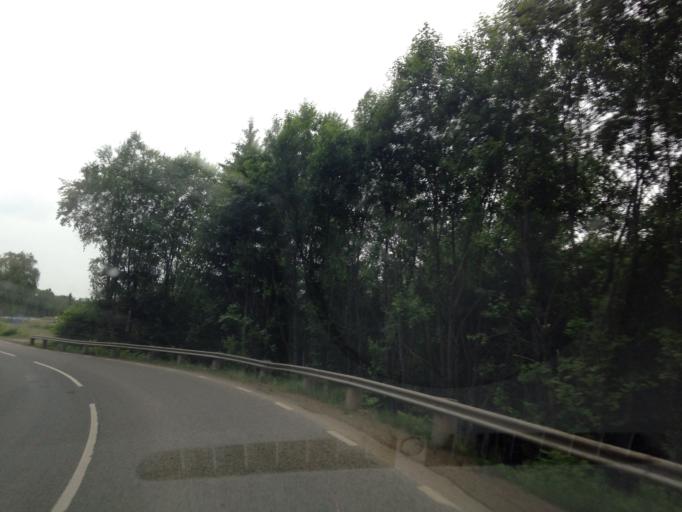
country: SE
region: Vaestra Goetaland
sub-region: Lerums Kommun
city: Lerum
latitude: 57.6877
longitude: 12.3164
